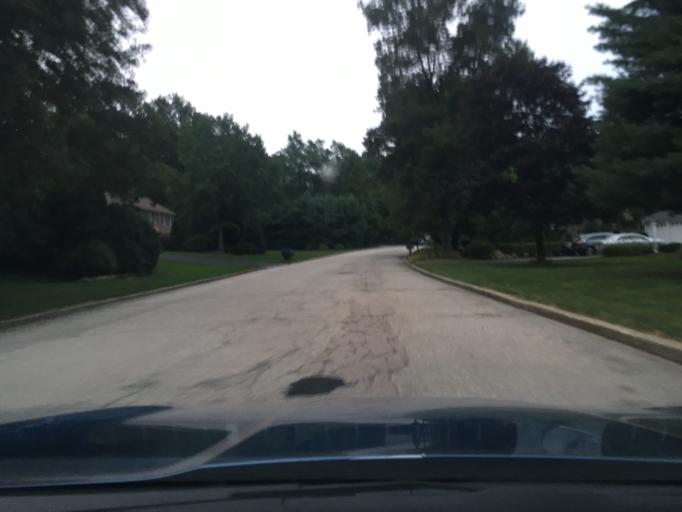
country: US
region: Rhode Island
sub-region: Kent County
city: West Warwick
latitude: 41.6601
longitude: -71.5140
